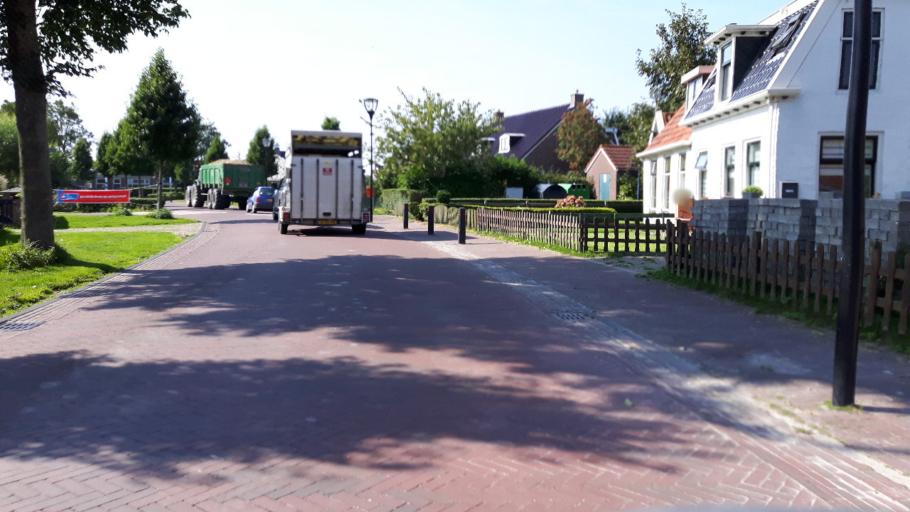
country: NL
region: Friesland
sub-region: Gemeente Franekeradeel
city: Franeker
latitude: 53.2081
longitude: 5.5439
